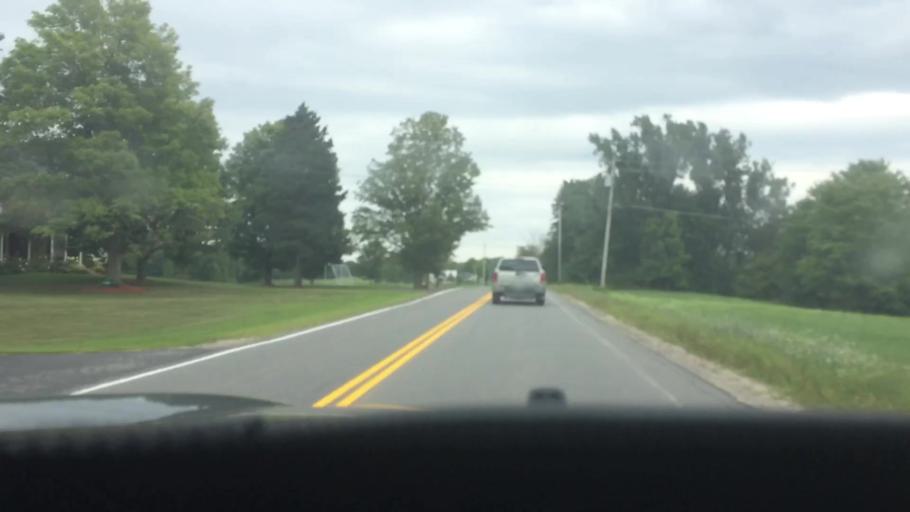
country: US
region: New York
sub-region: St. Lawrence County
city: Canton
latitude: 44.5275
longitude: -75.1897
